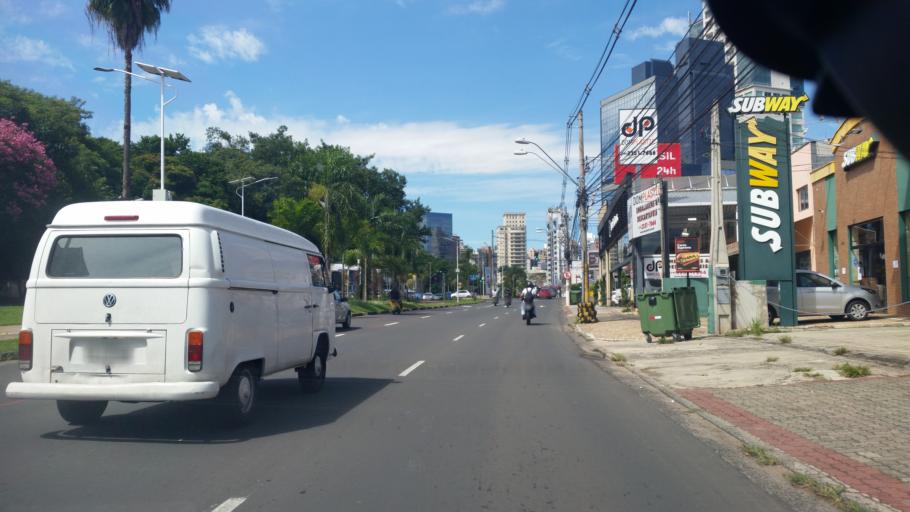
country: BR
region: Sao Paulo
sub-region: Campinas
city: Campinas
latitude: -22.8887
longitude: -47.0451
